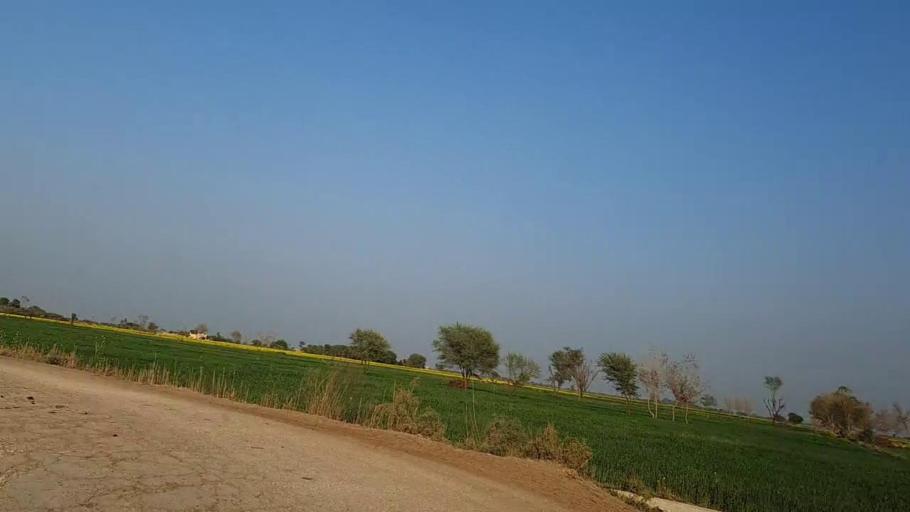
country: PK
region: Sindh
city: Sakrand
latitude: 26.1099
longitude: 68.3689
